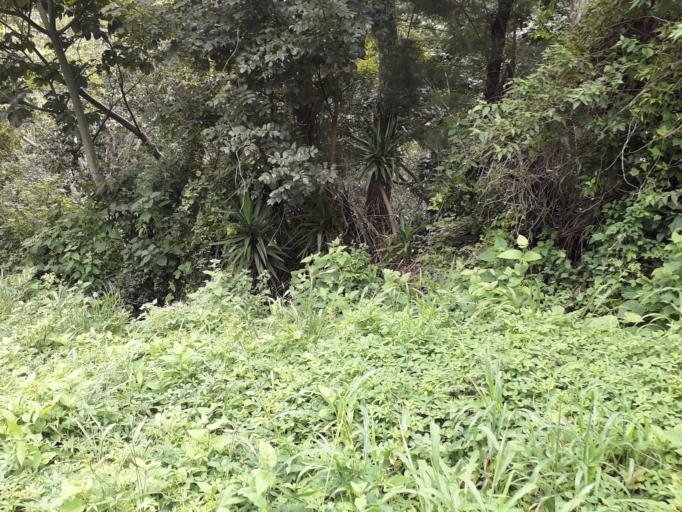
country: GT
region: Escuintla
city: Guanagazapa
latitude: 14.3115
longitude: -90.5595
